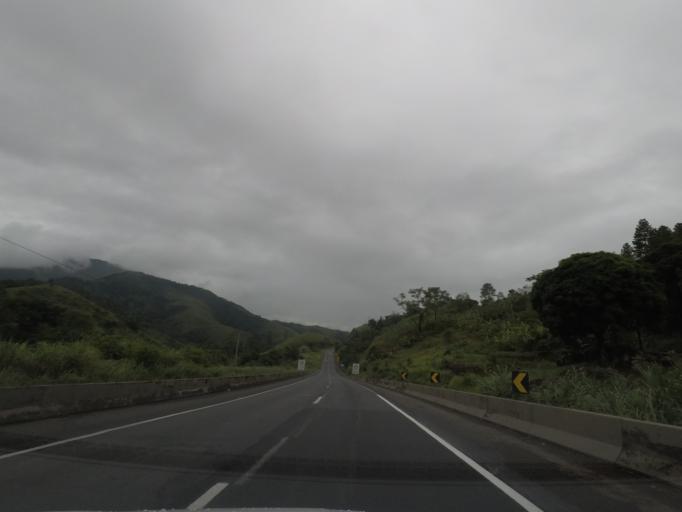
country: BR
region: Sao Paulo
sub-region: Cajati
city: Cajati
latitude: -24.8378
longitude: -48.2129
